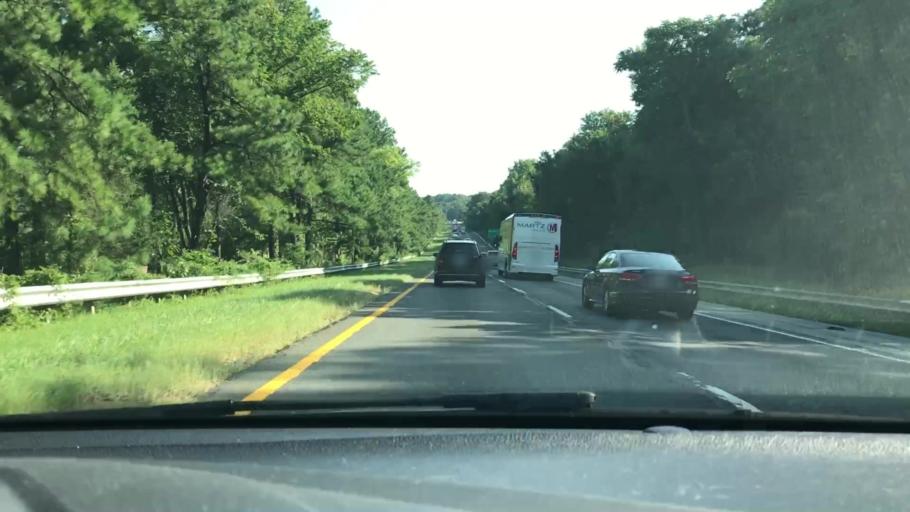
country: US
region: Maryland
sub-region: Prince George's County
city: Glassmanor
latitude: 38.8312
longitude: -77.0146
